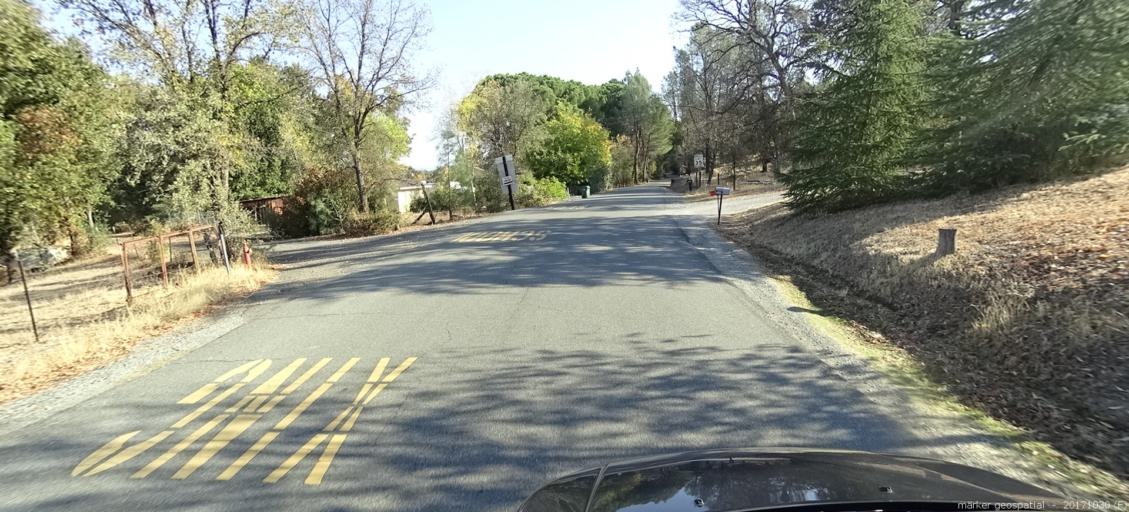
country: US
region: California
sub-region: Shasta County
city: Palo Cedro
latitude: 40.5522
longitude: -122.1676
